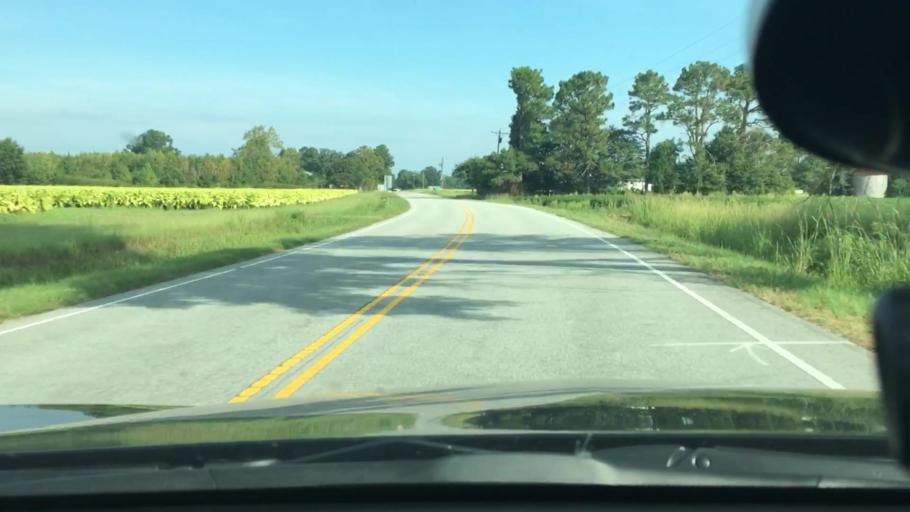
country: US
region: North Carolina
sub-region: Edgecombe County
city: Pinetops
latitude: 35.7460
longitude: -77.5409
